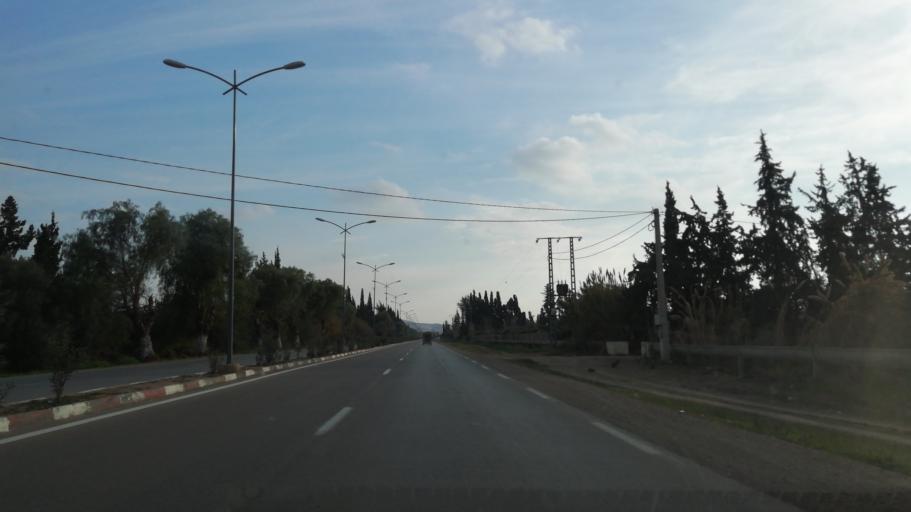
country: DZ
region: Mascara
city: Mascara
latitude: 35.6105
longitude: 0.0629
